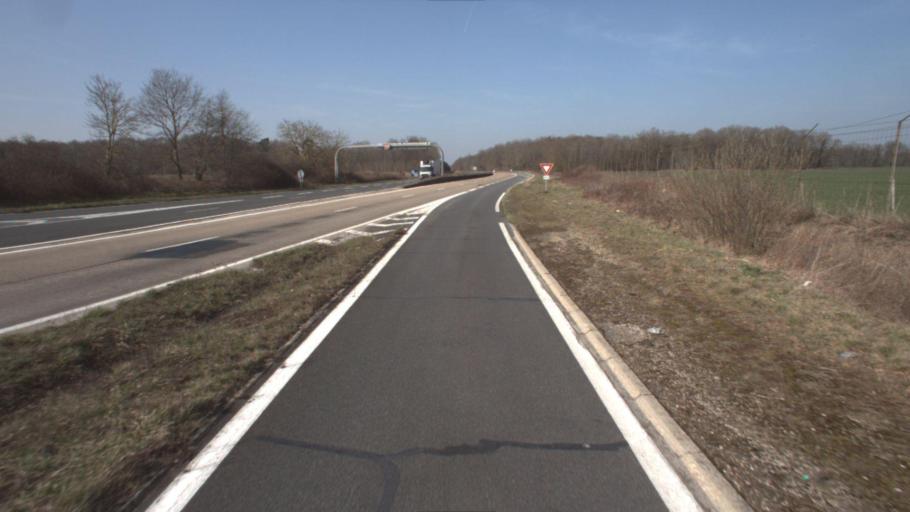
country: FR
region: Ile-de-France
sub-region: Departement de Seine-et-Marne
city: Cely
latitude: 48.4686
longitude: 2.5376
